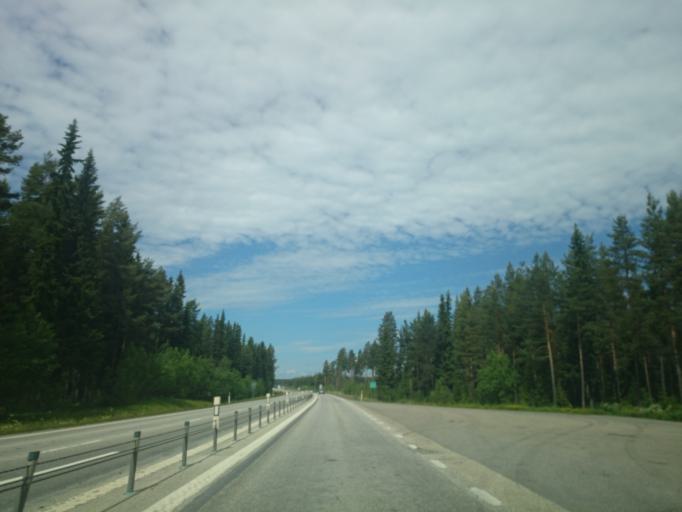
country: SE
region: Jaemtland
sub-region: OEstersunds Kommun
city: Brunflo
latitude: 63.1280
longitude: 14.7927
